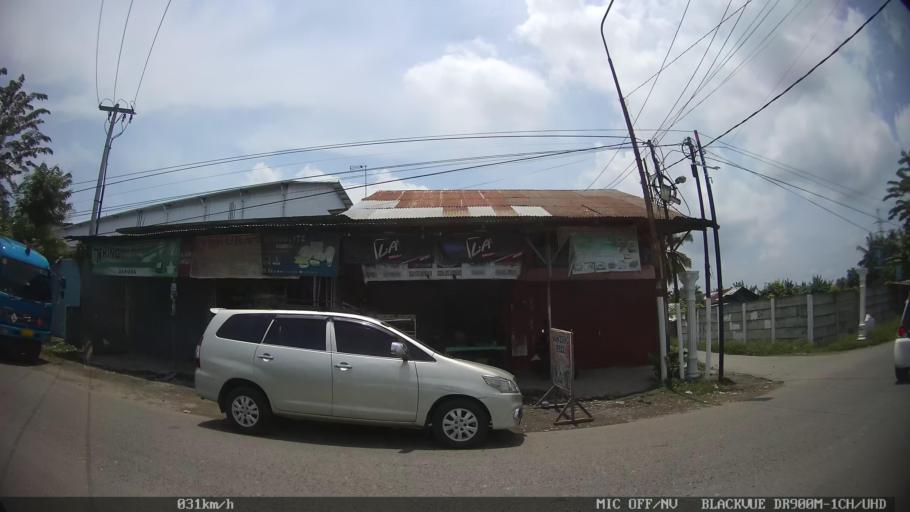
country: ID
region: North Sumatra
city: Labuhan Deli
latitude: 3.7194
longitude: 98.6683
